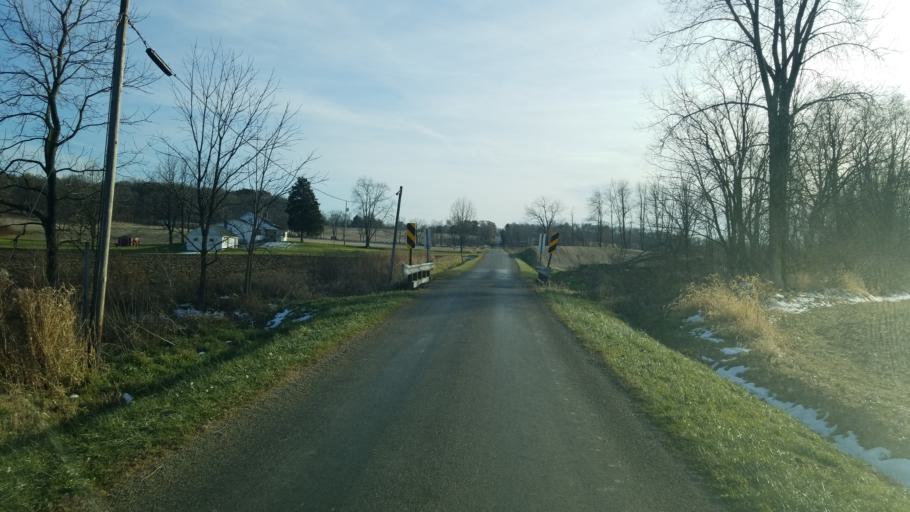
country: US
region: Ohio
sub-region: Ashland County
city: Ashland
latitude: 40.7693
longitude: -82.2879
